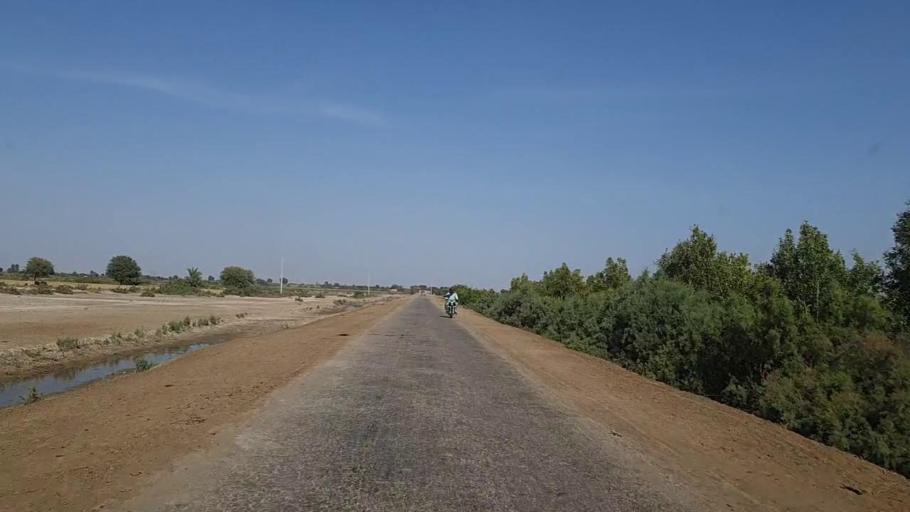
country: PK
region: Sindh
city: Kotri
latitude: 25.1611
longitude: 68.2505
